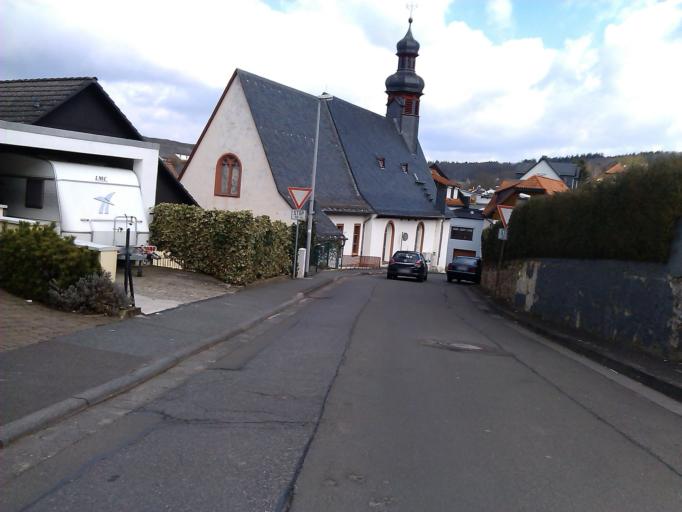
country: DE
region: Rheinland-Pfalz
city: Bingen am Rhein
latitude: 49.9934
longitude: 7.8903
